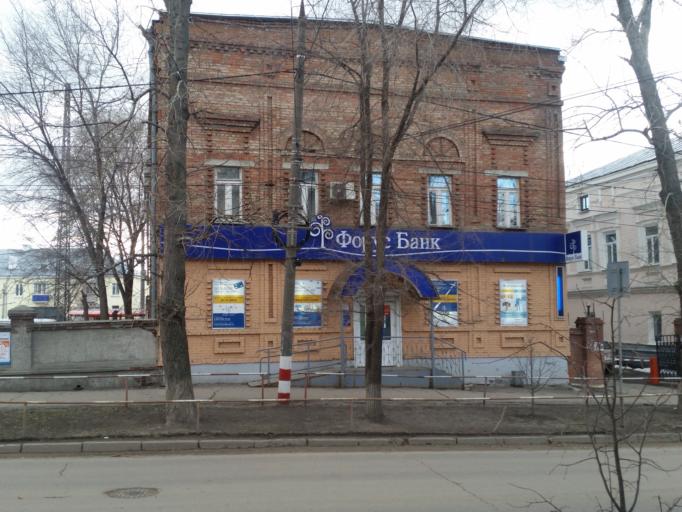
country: RU
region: Ulyanovsk
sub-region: Ulyanovskiy Rayon
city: Ulyanovsk
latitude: 54.3142
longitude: 48.3888
